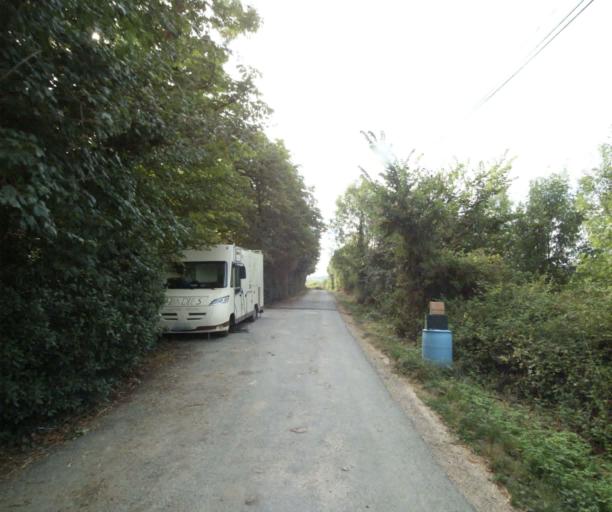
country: FR
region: Midi-Pyrenees
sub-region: Departement du Tarn
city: Puylaurens
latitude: 43.5354
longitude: 2.0461
